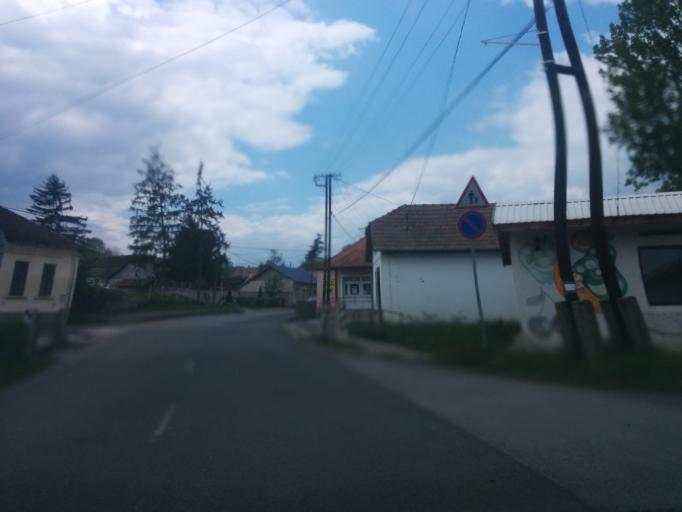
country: HU
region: Nograd
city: Bujak
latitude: 47.8275
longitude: 19.5331
